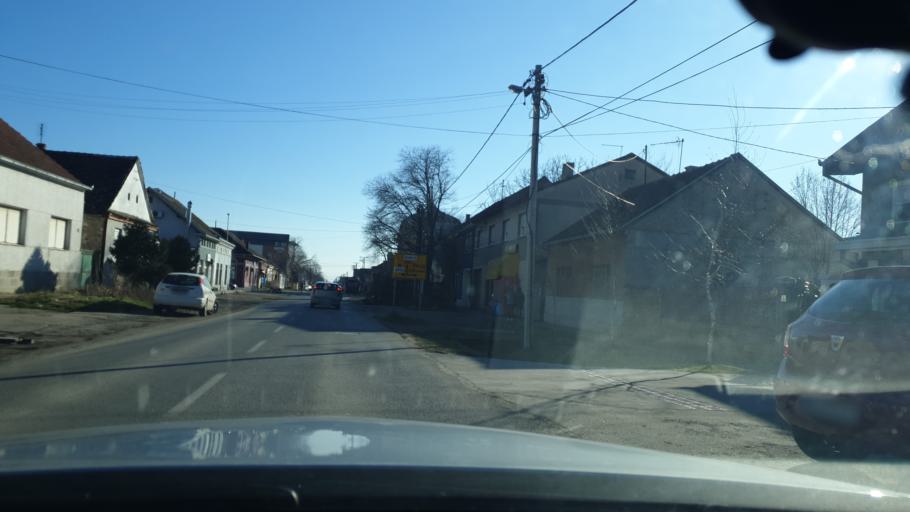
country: RS
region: Autonomna Pokrajina Vojvodina
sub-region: Sremski Okrug
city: Ruma
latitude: 45.0089
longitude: 19.8160
